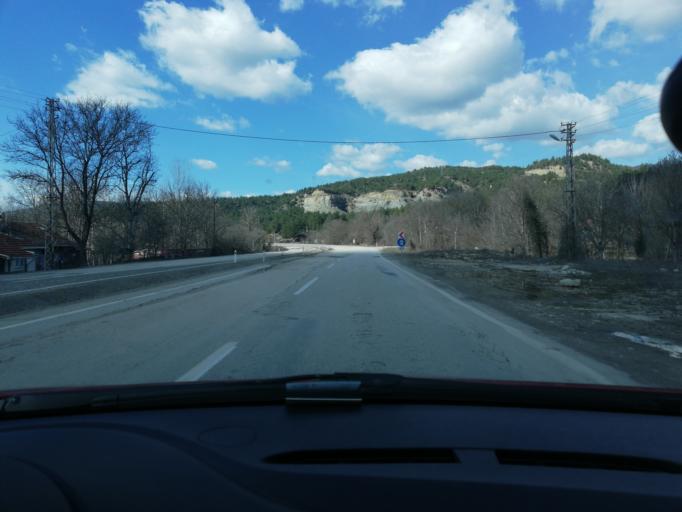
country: TR
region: Karabuk
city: Ovacik
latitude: 41.2026
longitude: 32.9080
